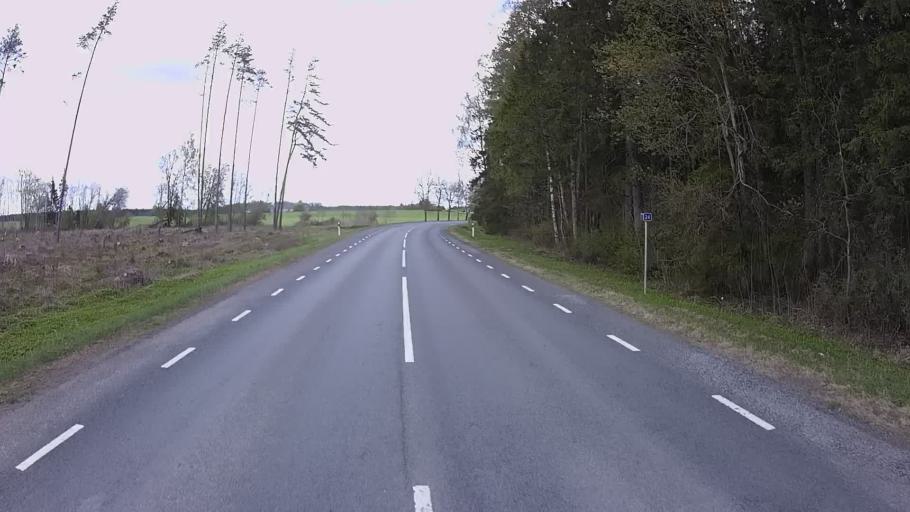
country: EE
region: Jaervamaa
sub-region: Koeru vald
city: Koeru
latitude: 58.9727
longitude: 26.0357
